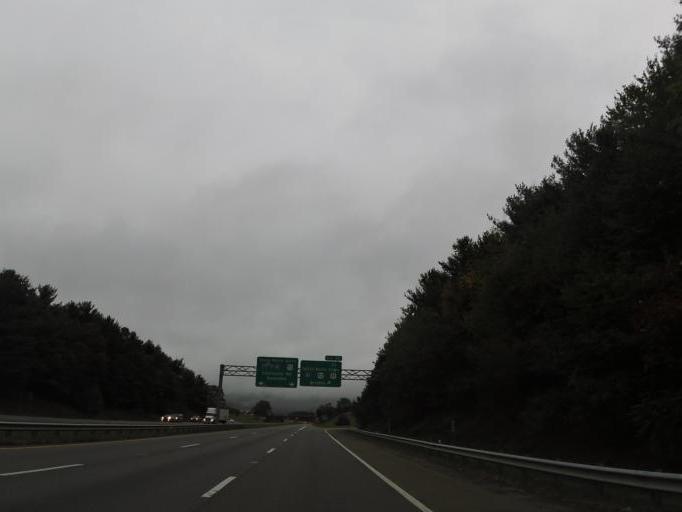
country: US
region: Virginia
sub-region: Wythe County
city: Wytheville
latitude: 36.9657
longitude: -81.0661
